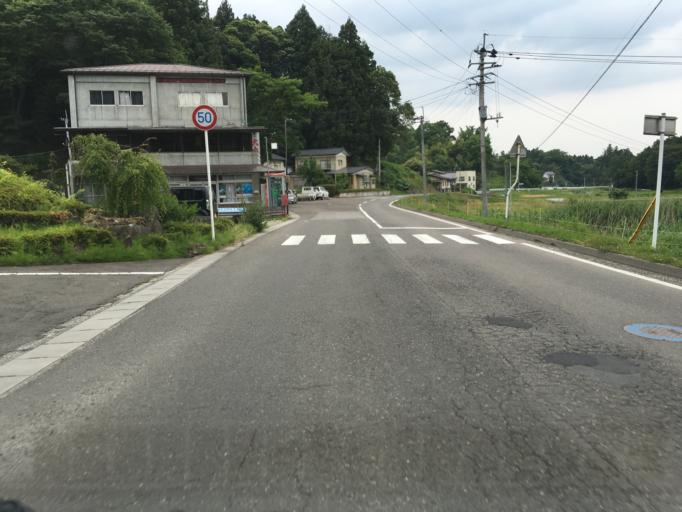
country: JP
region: Fukushima
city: Nihommatsu
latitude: 37.6378
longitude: 140.5368
